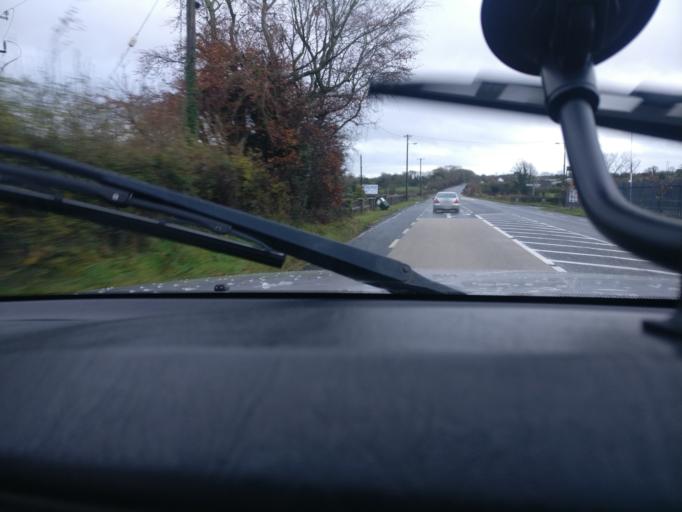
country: IE
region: Leinster
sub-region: Kildare
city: Kilcock
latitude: 53.4203
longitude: -6.7369
